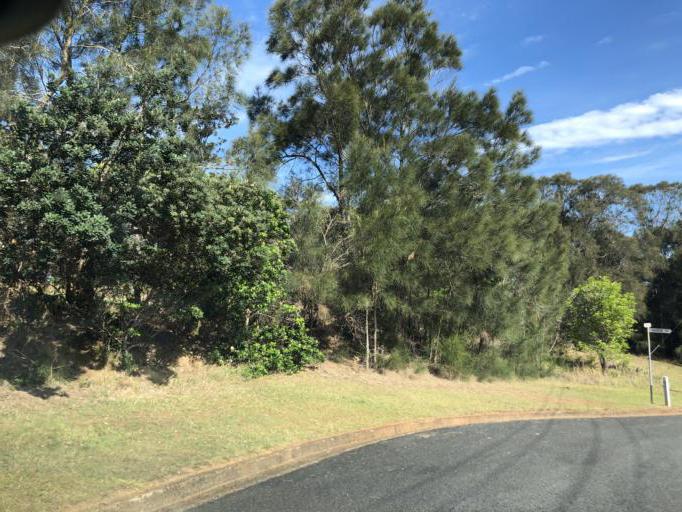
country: AU
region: New South Wales
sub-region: Coffs Harbour
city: Moonee Beach
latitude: -30.2354
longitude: 153.1516
